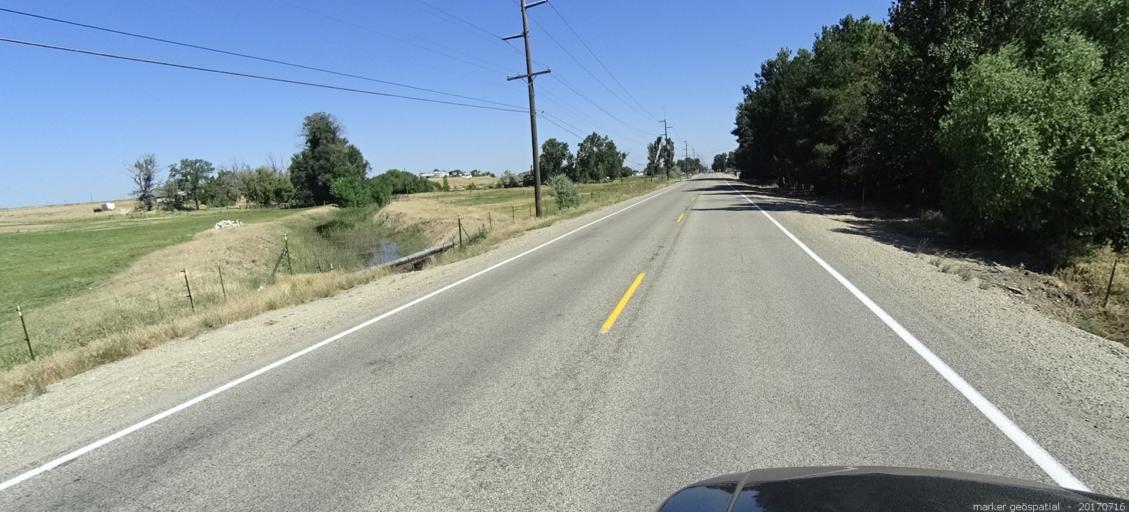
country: US
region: Idaho
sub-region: Ada County
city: Kuna
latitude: 43.5262
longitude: -116.3344
